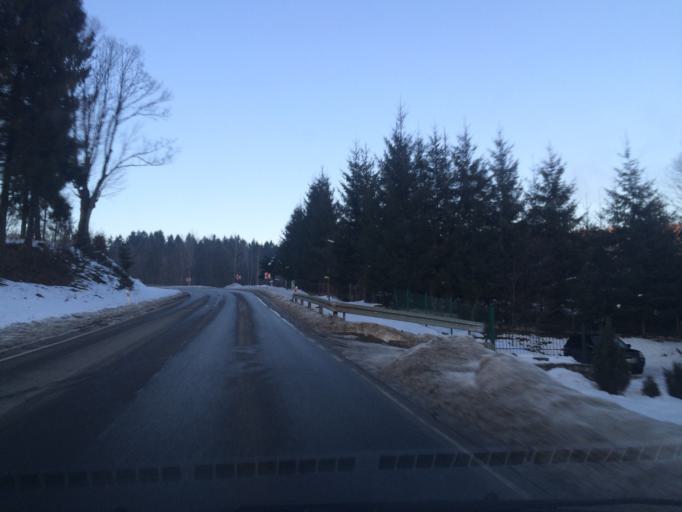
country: PL
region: Subcarpathian Voivodeship
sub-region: Powiat bieszczadzki
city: Czarna
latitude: 49.3473
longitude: 22.6825
